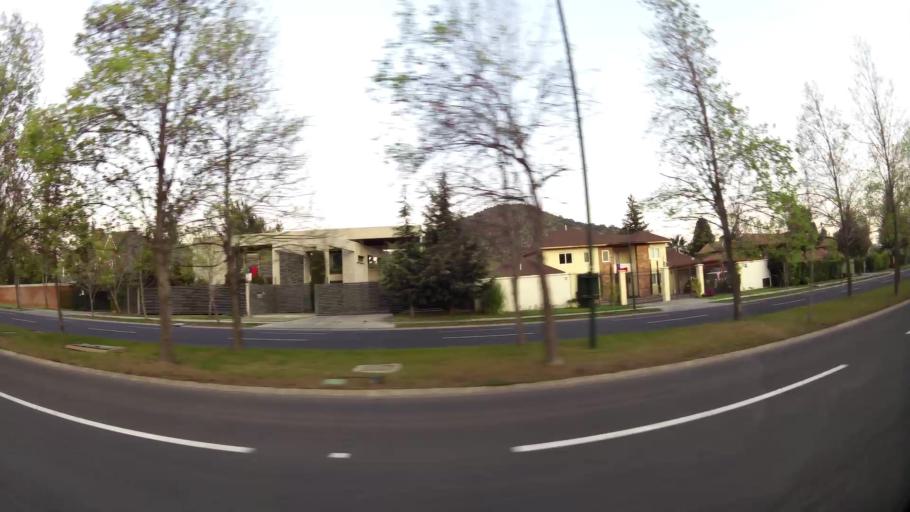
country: CL
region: Santiago Metropolitan
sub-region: Provincia de Chacabuco
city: Chicureo Abajo
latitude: -33.3359
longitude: -70.5455
